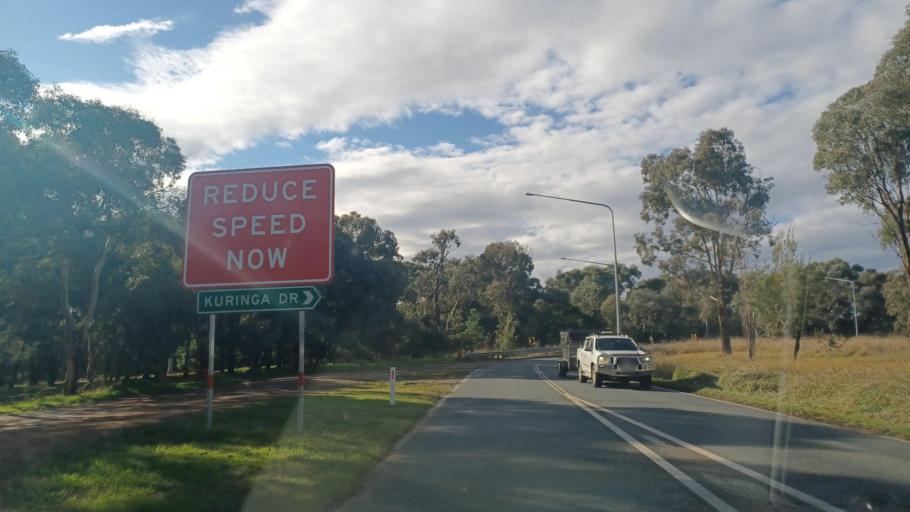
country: AU
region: Australian Capital Territory
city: Belconnen
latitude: -35.1881
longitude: 149.0477
